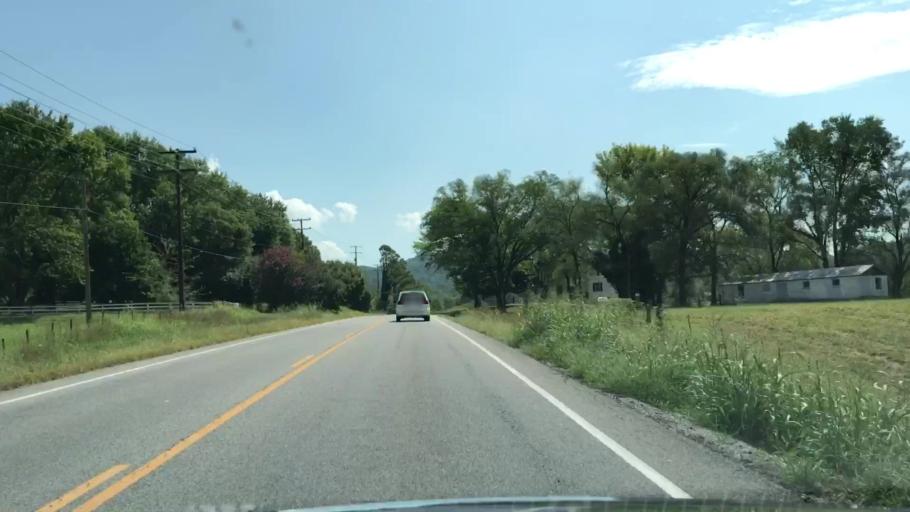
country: US
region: Tennessee
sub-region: Trousdale County
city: Hartsville
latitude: 36.3841
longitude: -86.1236
